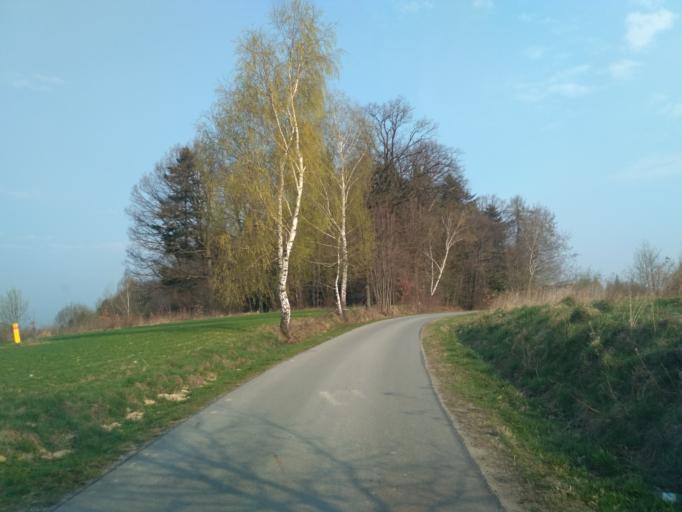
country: PL
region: Subcarpathian Voivodeship
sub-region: Powiat strzyzowski
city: Wisniowa
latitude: 49.8799
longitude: 21.6357
